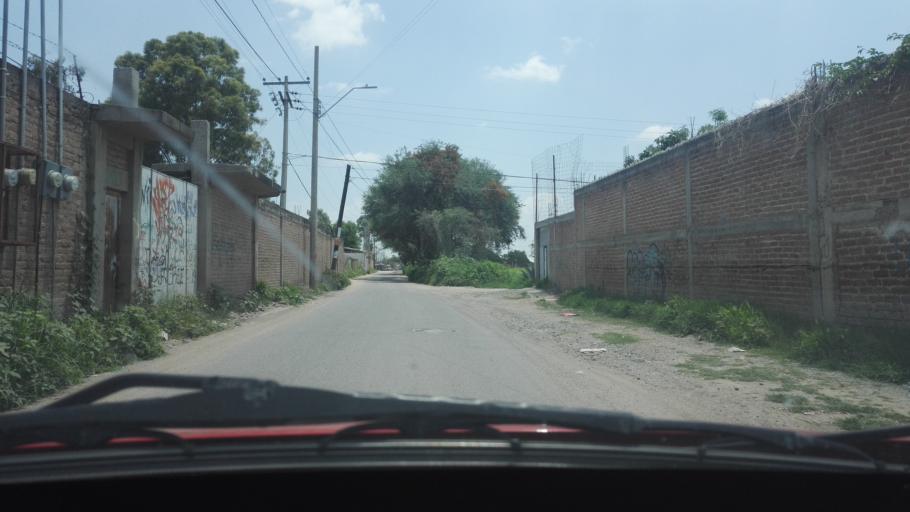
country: MX
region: Guanajuato
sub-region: Leon
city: Fraccionamiento Paraiso Real
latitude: 21.0754
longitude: -101.6092
